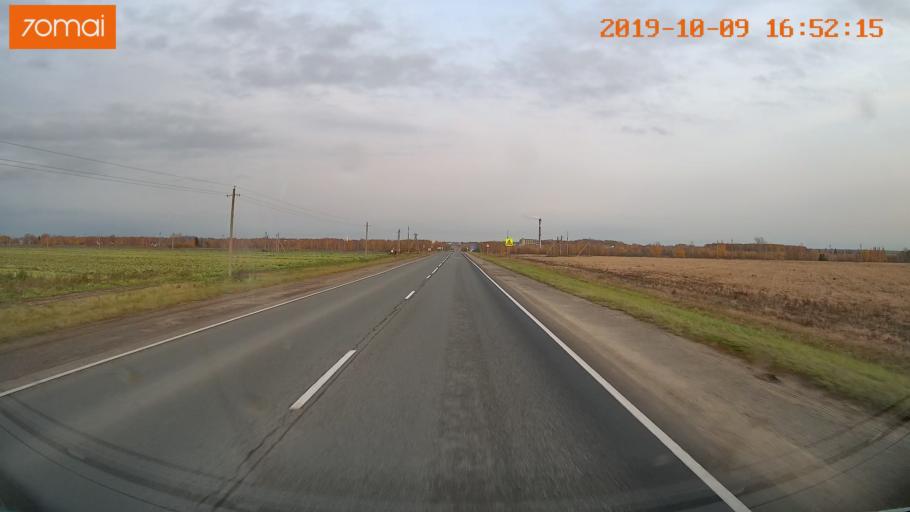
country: RU
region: Ivanovo
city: Privolzhsk
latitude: 57.3814
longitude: 41.2421
